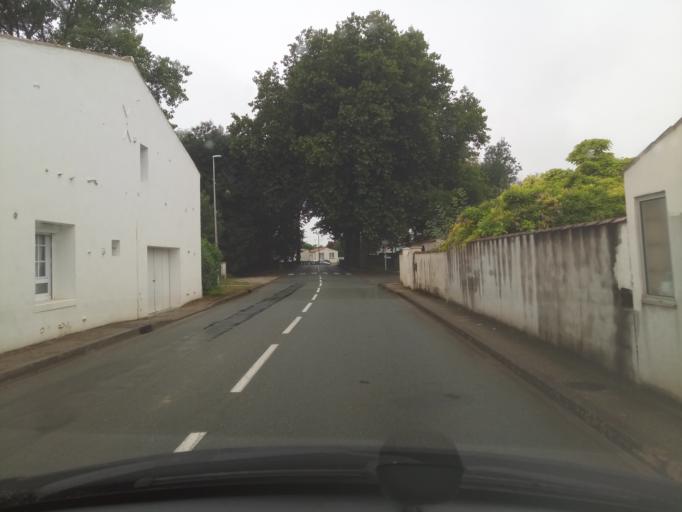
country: FR
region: Poitou-Charentes
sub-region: Departement de la Charente-Maritime
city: Andilly
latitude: 46.2298
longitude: -0.9942
